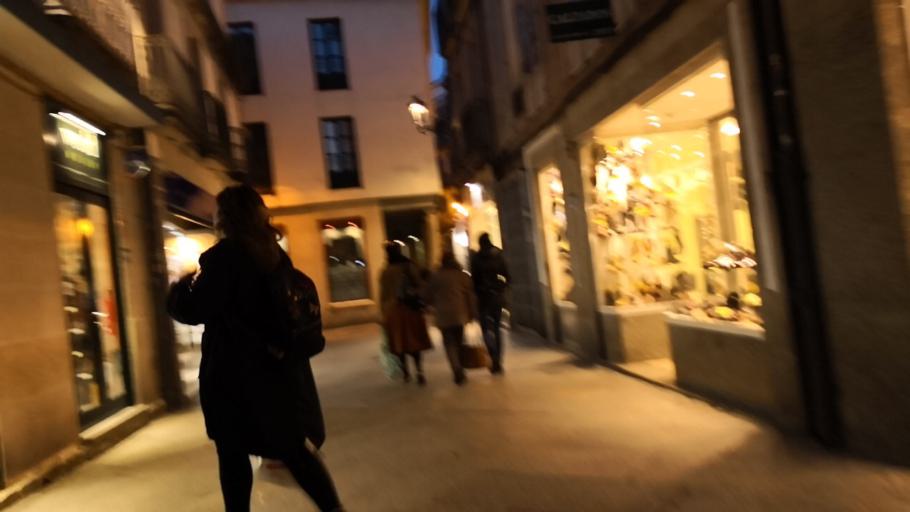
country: ES
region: Galicia
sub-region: Provincia de Ourense
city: Ourense
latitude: 42.3374
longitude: -7.8635
